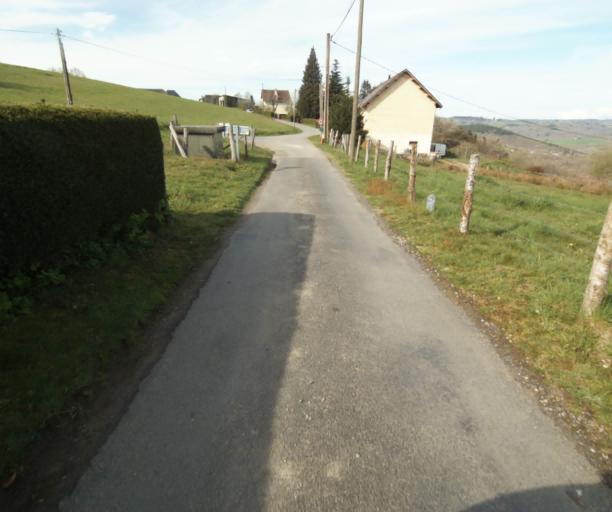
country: FR
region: Limousin
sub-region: Departement de la Correze
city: Correze
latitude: 45.3403
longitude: 1.8317
